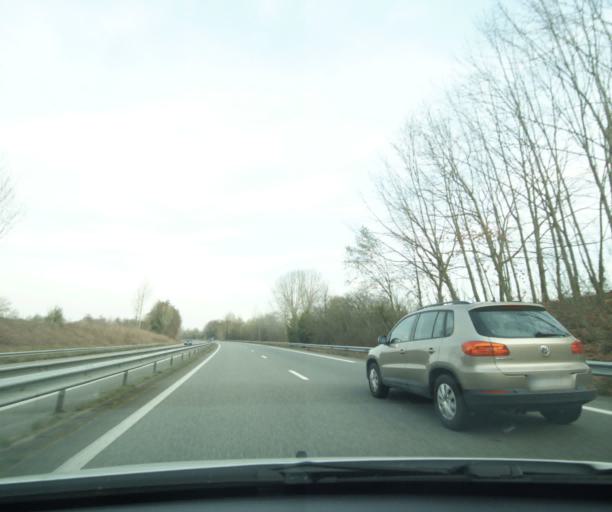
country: FR
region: Midi-Pyrenees
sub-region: Departement des Hautes-Pyrenees
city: Odos
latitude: 43.2087
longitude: 0.0482
